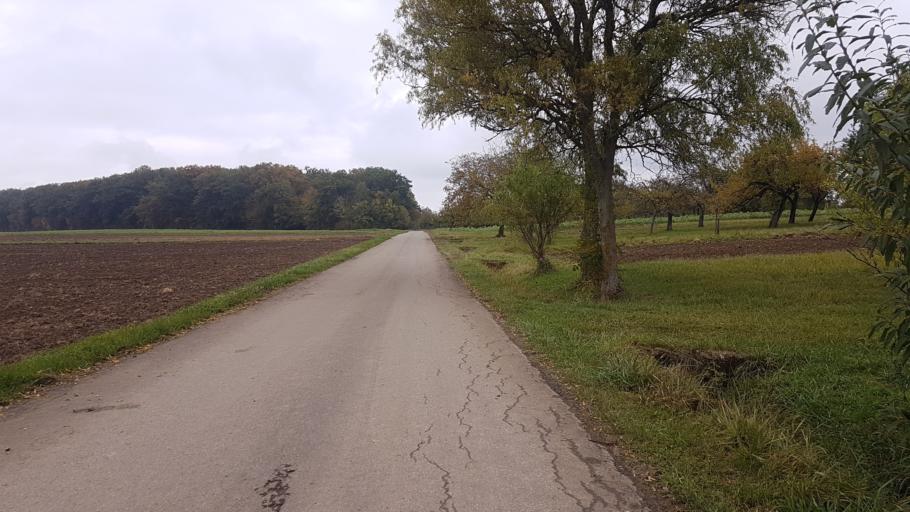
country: DE
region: Baden-Wuerttemberg
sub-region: Tuebingen Region
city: Dusslingen
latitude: 48.4538
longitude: 9.0354
